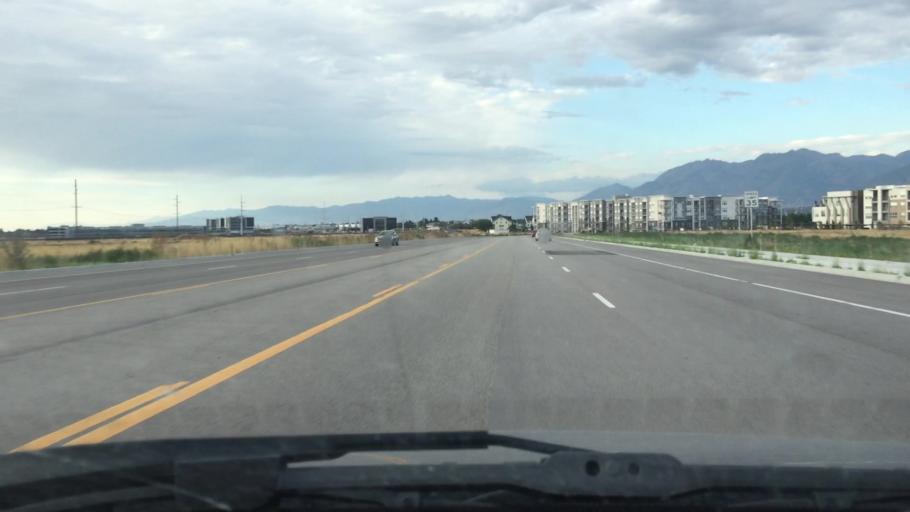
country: US
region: Utah
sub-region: Salt Lake County
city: Bluffdale
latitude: 40.5033
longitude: -111.9078
